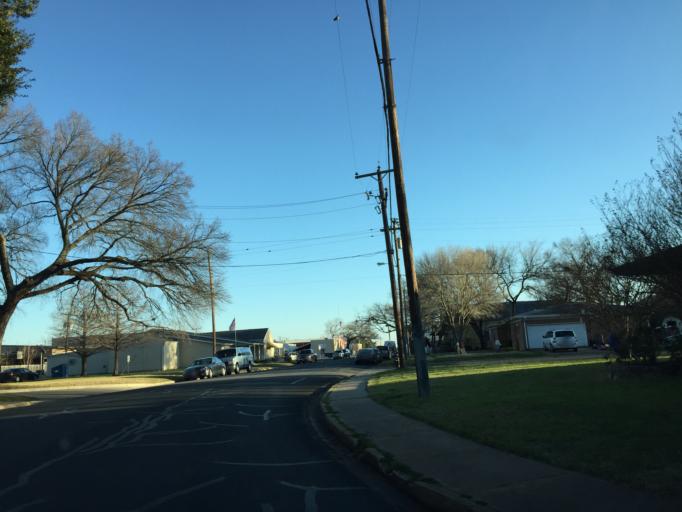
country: US
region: Texas
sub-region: Bastrop County
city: Elgin
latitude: 30.3503
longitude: -97.3727
